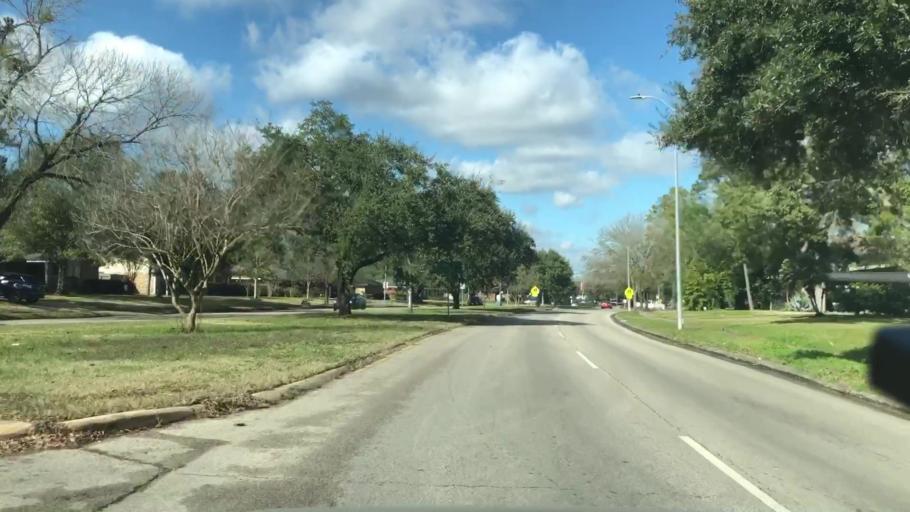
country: US
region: Texas
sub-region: Harris County
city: Bellaire
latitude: 29.6648
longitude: -95.4676
